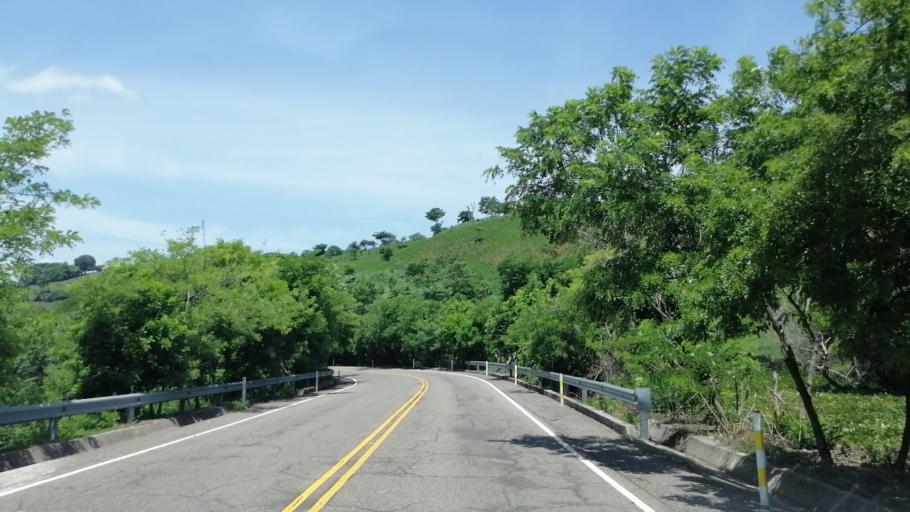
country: SV
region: Chalatenango
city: Nueva Concepcion
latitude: 14.1736
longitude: -89.3102
